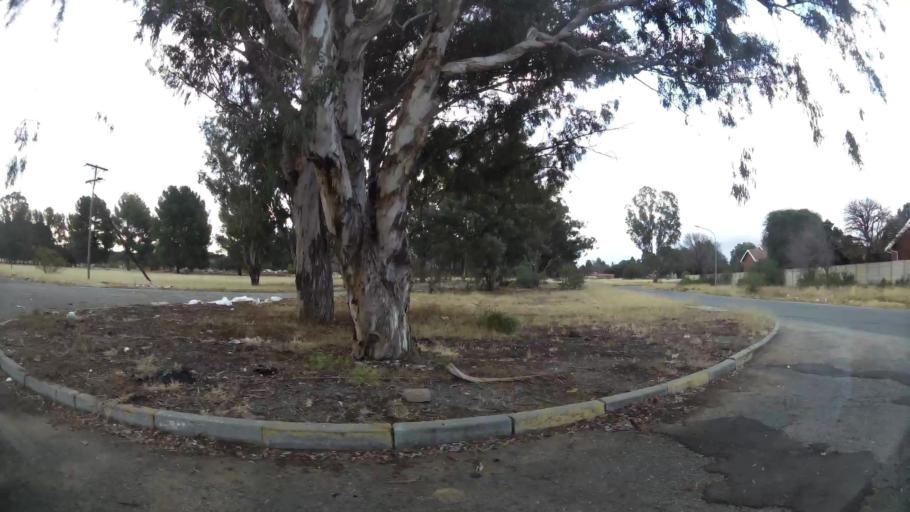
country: ZA
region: Orange Free State
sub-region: Lejweleputswa District Municipality
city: Welkom
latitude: -27.9996
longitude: 26.7197
